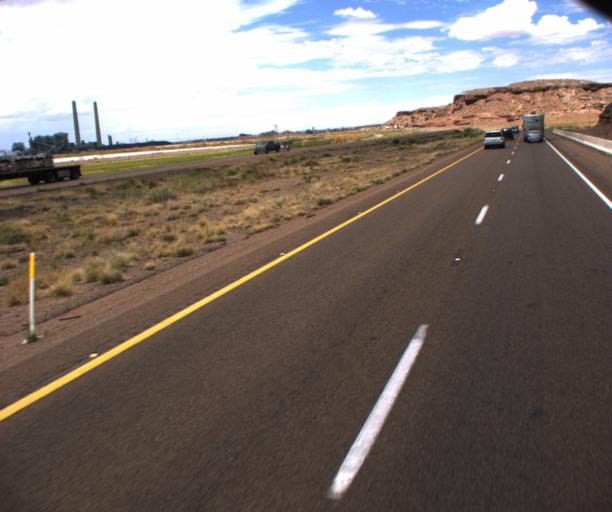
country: US
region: Arizona
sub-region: Navajo County
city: Joseph City
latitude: 34.9371
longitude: -110.2774
